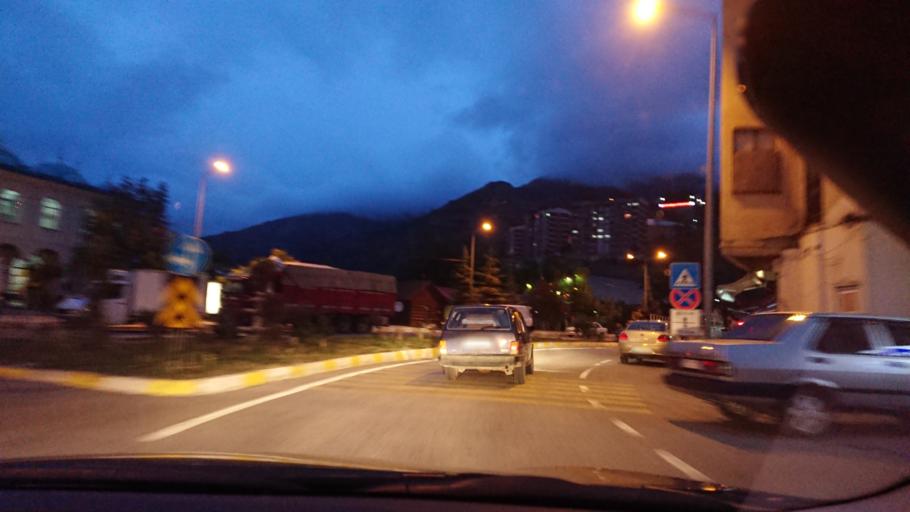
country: TR
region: Gumushane
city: Kurtun
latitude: 40.6696
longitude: 39.1394
